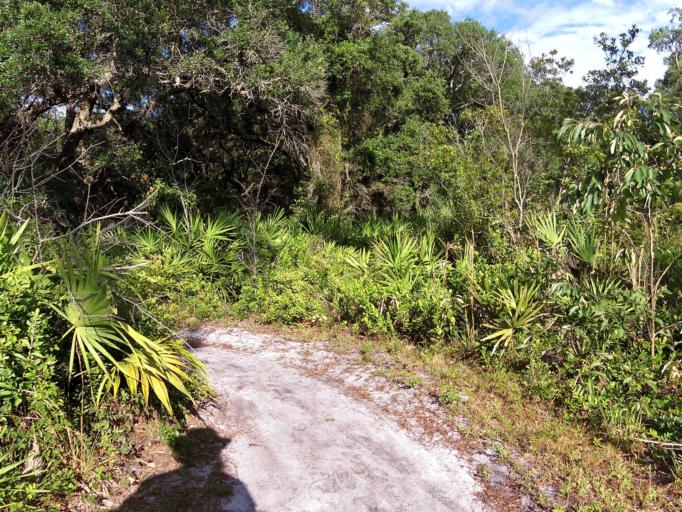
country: US
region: Florida
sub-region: Saint Johns County
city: Villano Beach
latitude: 30.0243
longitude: -81.3419
